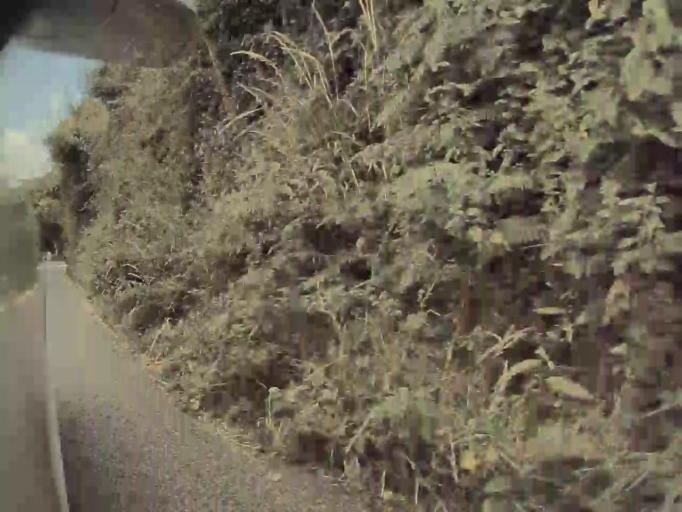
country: IE
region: Leinster
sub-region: Wicklow
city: Kilmacanoge
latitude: 53.1435
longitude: -6.1308
